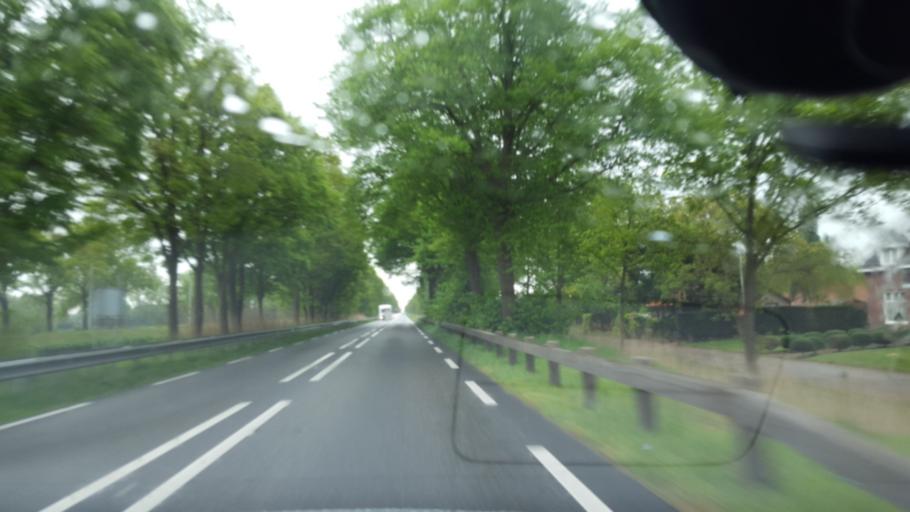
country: NL
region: North Brabant
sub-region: Gemeente Someren
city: Someren
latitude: 51.3495
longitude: 5.7431
